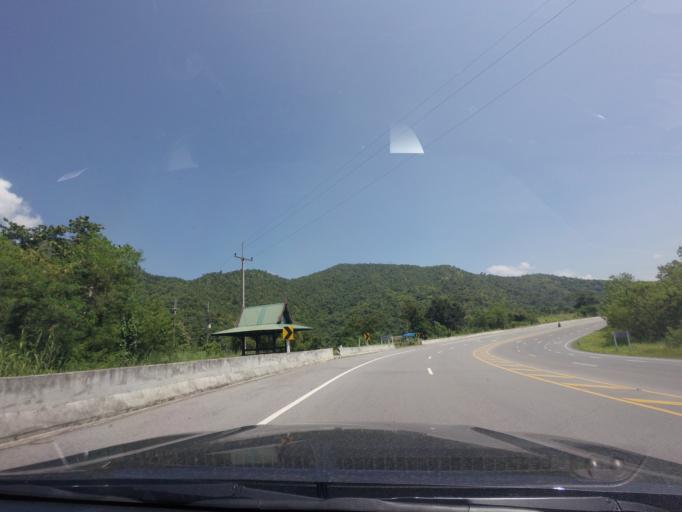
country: TH
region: Phetchabun
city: Lom Sak
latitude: 16.7736
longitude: 101.1306
